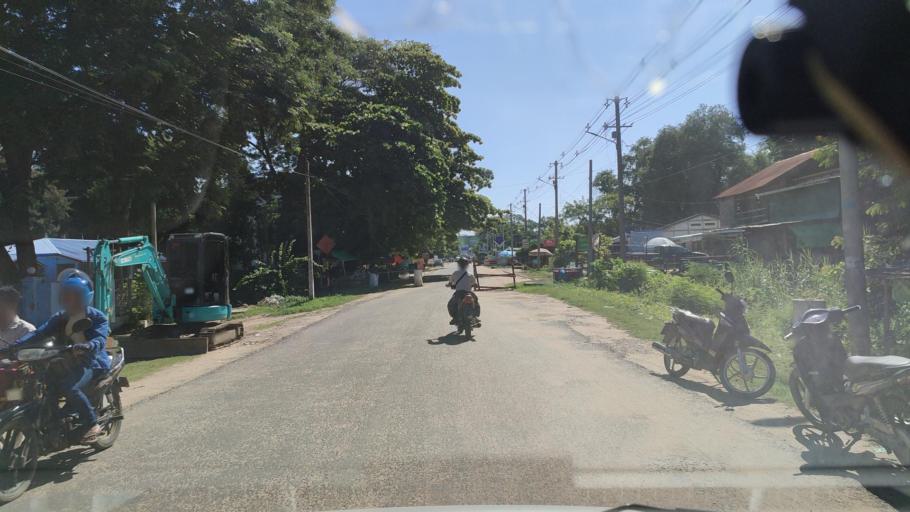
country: MM
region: Magway
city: Taungdwingyi
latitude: 20.0037
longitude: 95.5390
